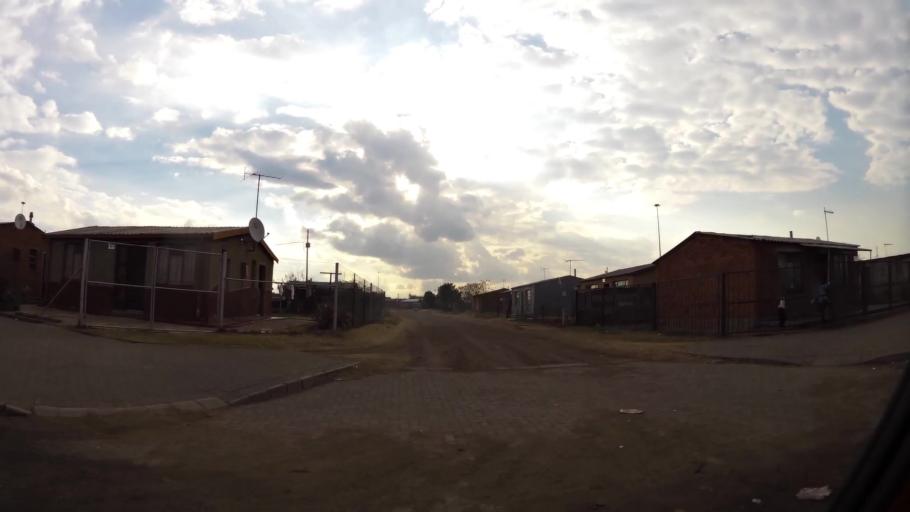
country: ZA
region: Gauteng
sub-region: Sedibeng District Municipality
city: Vanderbijlpark
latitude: -26.6956
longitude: 27.8770
